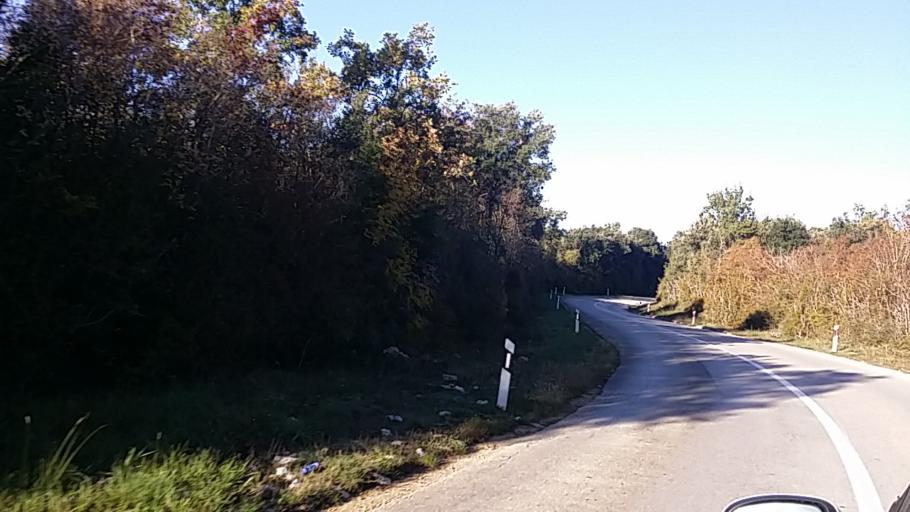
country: HR
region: Istarska
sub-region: Grad Rovinj
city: Rovinj
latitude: 45.1404
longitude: 13.7187
